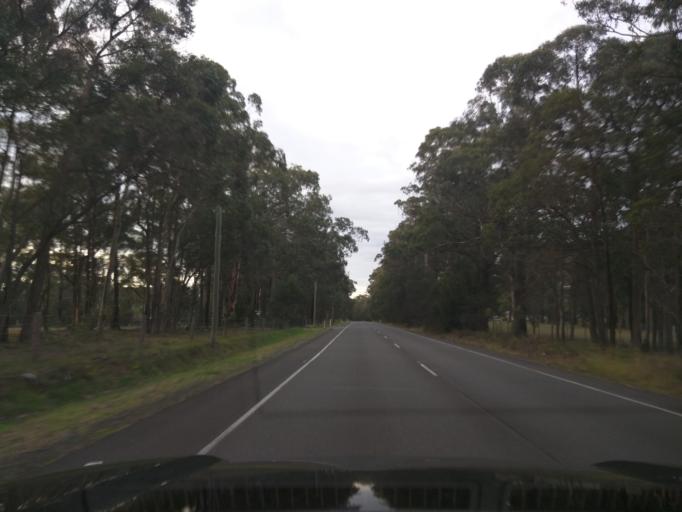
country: AU
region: New South Wales
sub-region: Wollondilly
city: Douglas Park
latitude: -34.2473
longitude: 150.7262
